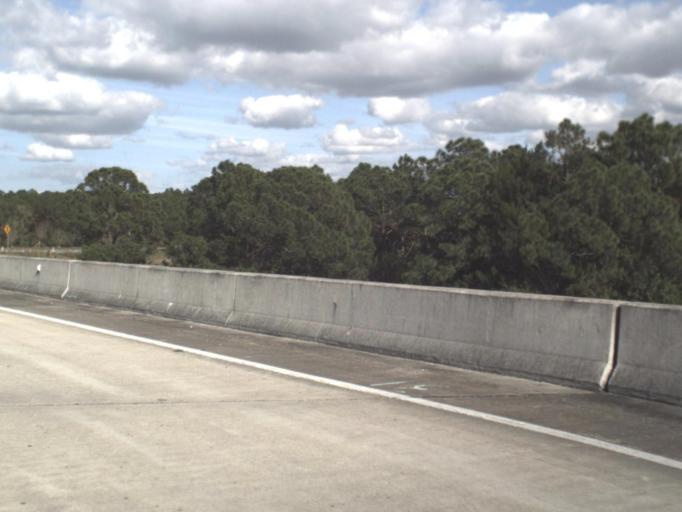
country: US
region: Florida
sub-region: Brevard County
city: Port Saint John
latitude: 28.5015
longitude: -80.8387
